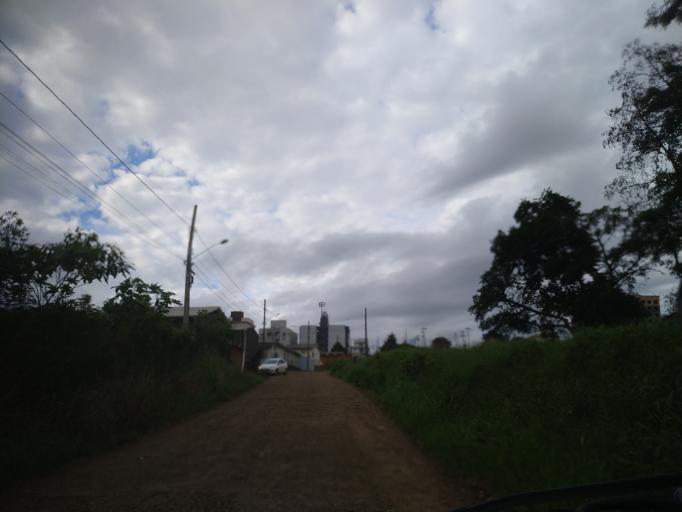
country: BR
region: Santa Catarina
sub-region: Chapeco
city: Chapeco
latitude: -27.0683
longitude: -52.6118
